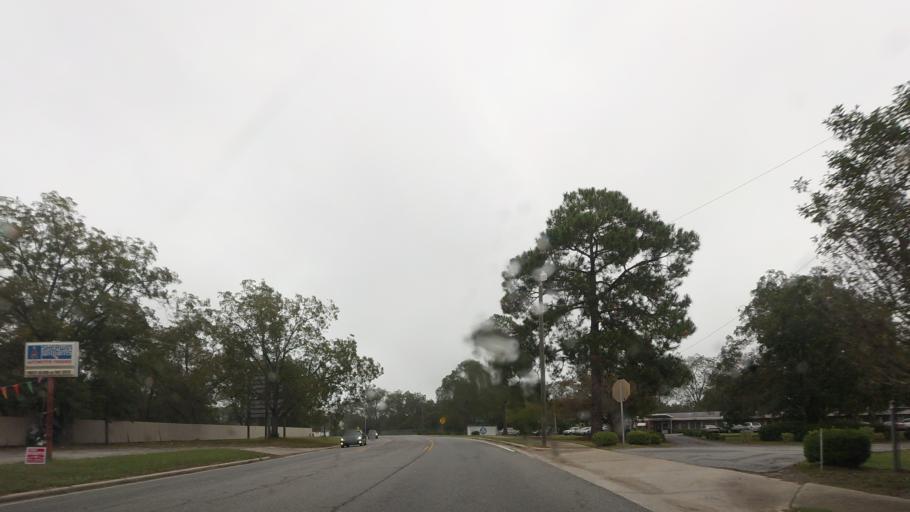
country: US
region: Georgia
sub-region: Ben Hill County
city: Fitzgerald
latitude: 31.7285
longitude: -83.2476
